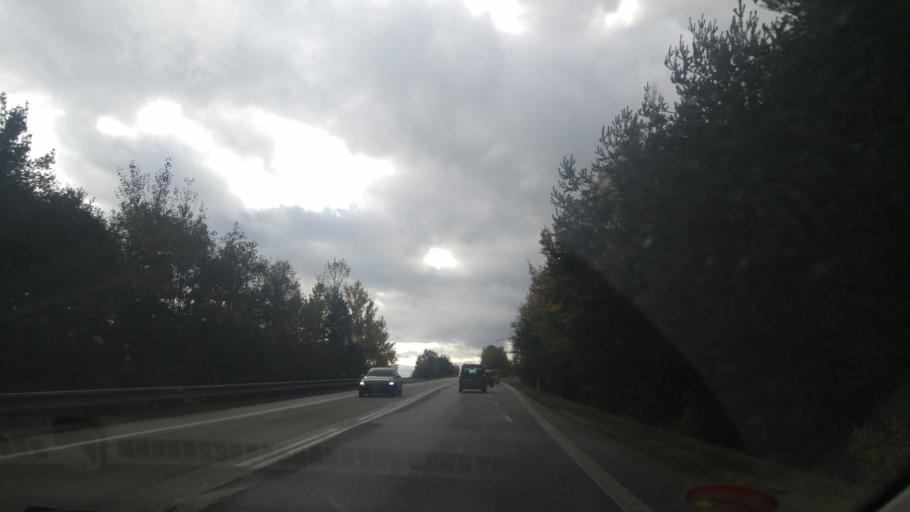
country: CZ
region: Jihocesky
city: Sevetin
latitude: 49.0730
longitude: 14.5395
